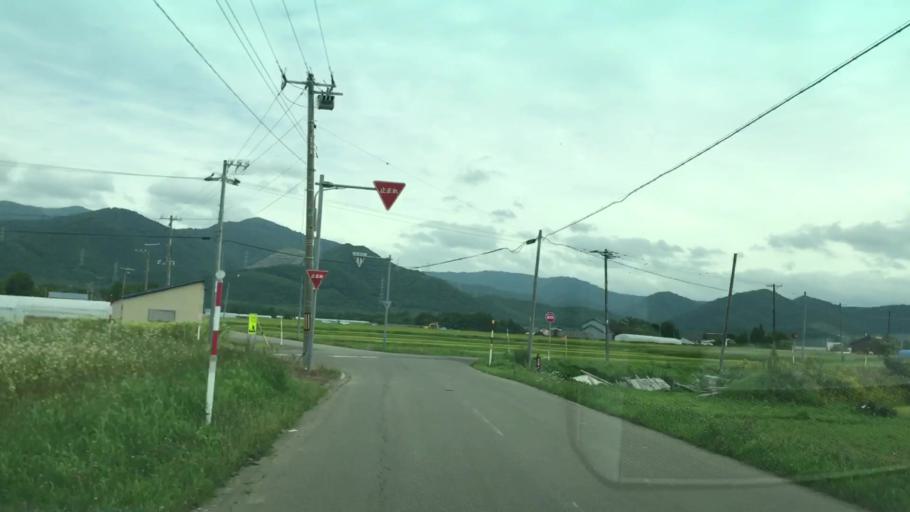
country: JP
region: Hokkaido
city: Iwanai
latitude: 43.0306
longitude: 140.5709
